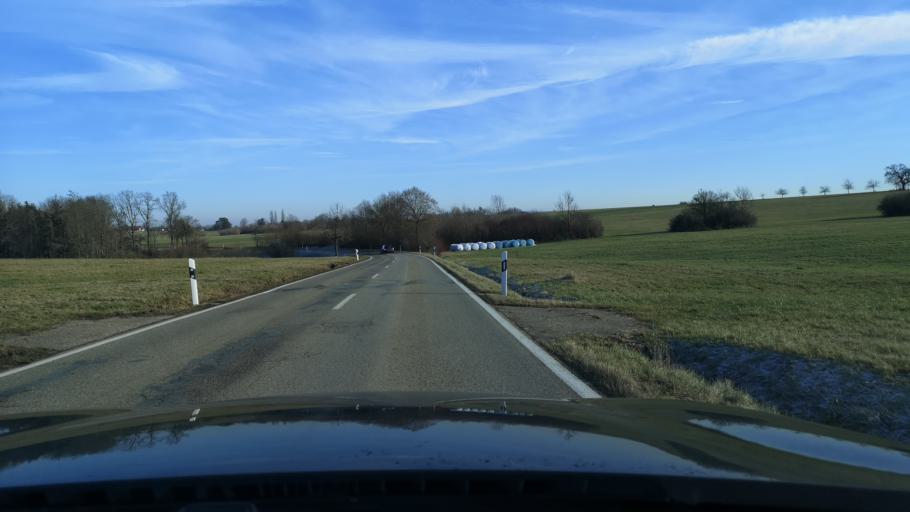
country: DE
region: Baden-Wuerttemberg
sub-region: Regierungsbezirk Stuttgart
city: Obergroningen
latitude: 48.8926
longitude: 9.9207
